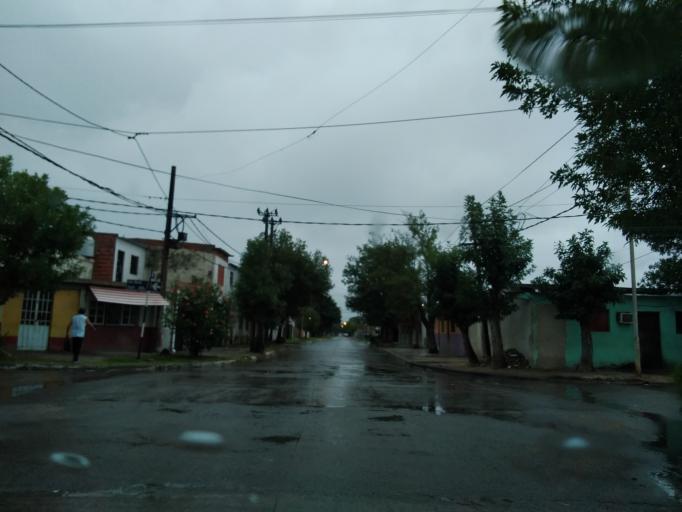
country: AR
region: Corrientes
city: Corrientes
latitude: -27.4821
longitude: -58.8241
